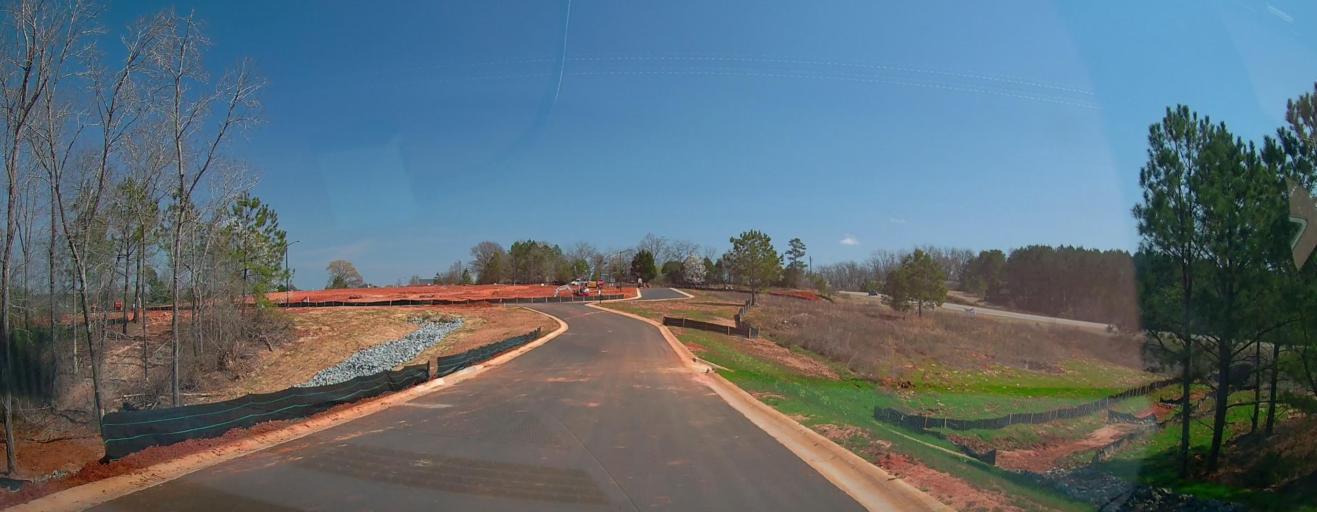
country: US
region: Georgia
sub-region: Peach County
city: Byron
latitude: 32.6072
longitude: -83.7658
